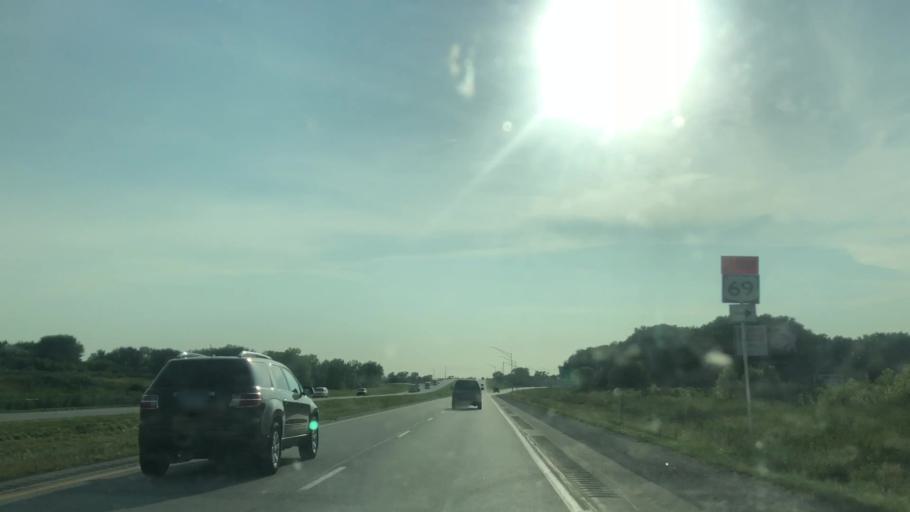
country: US
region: Iowa
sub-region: Story County
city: Ames
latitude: 42.0058
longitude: -93.6004
